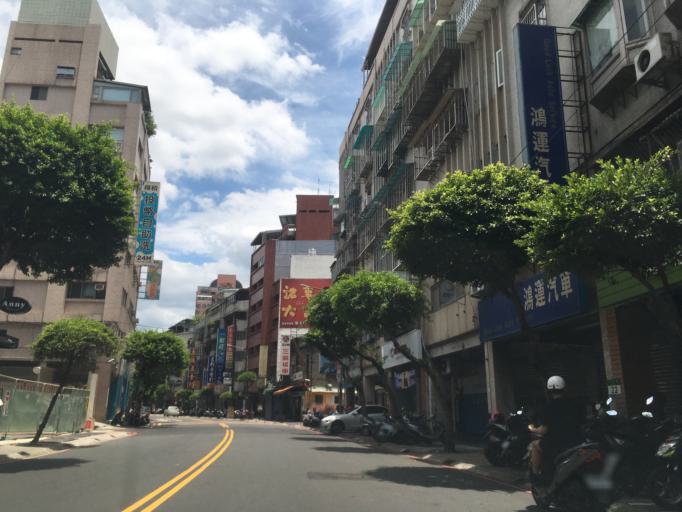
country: TW
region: Taipei
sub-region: Taipei
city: Banqiao
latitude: 25.0004
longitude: 121.5152
